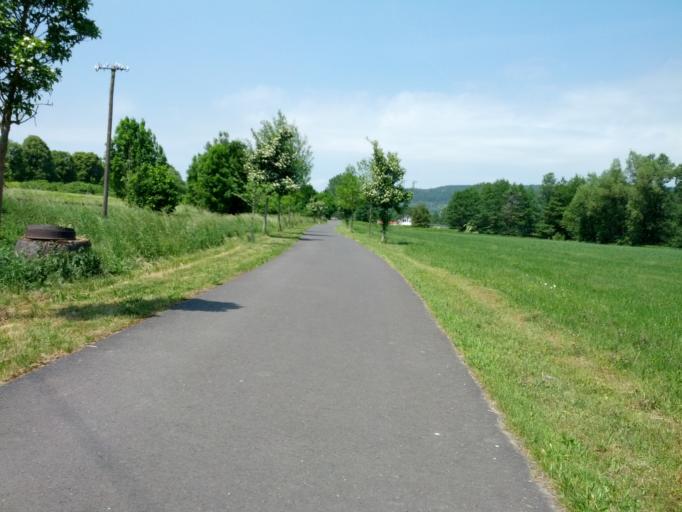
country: DE
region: Thuringia
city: Weilar
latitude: 50.7718
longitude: 10.1387
